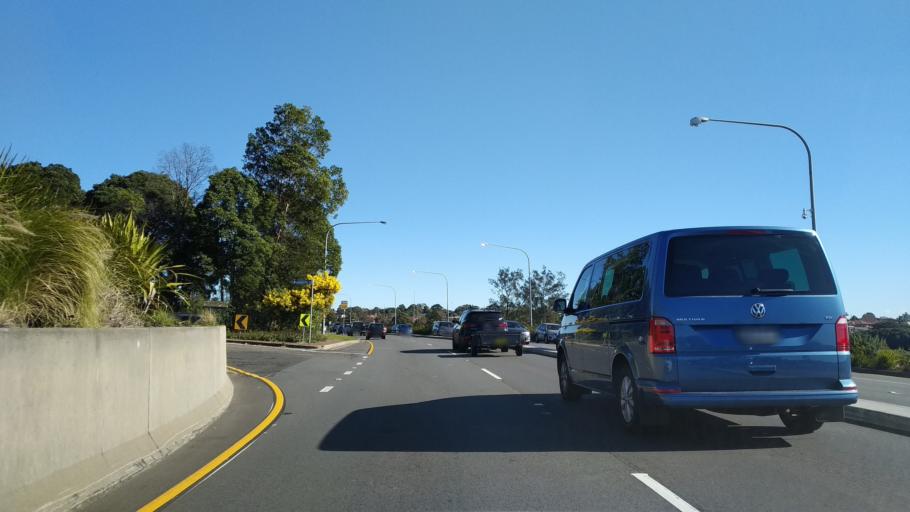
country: AU
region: New South Wales
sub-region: Leichhardt
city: Leichhardt
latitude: -33.8700
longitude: 151.1462
